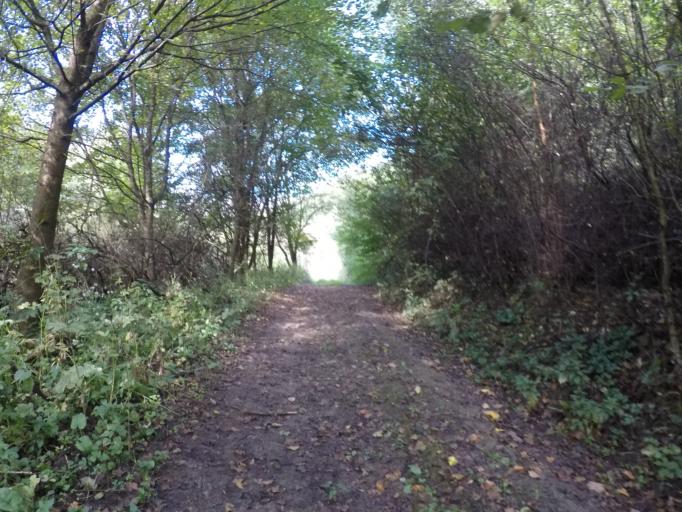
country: SK
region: Presovsky
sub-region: Okres Presov
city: Presov
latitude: 48.9321
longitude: 21.1654
